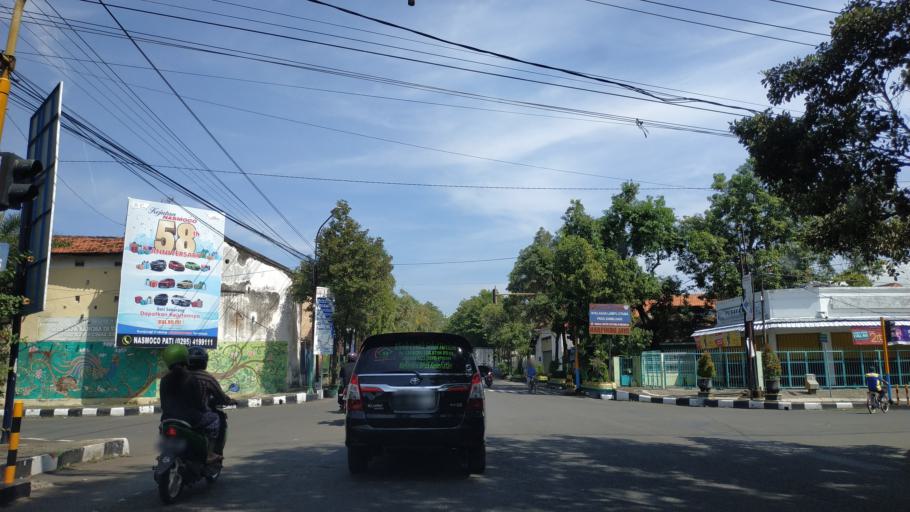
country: ID
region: Central Java
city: Pati
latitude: -6.7542
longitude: 111.0442
